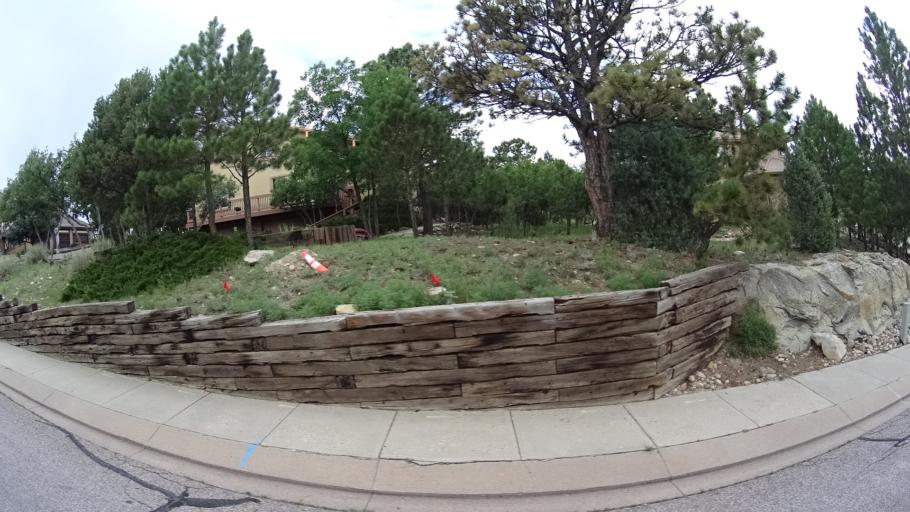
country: US
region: Colorado
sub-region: El Paso County
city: Colorado Springs
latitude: 38.9058
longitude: -104.8489
